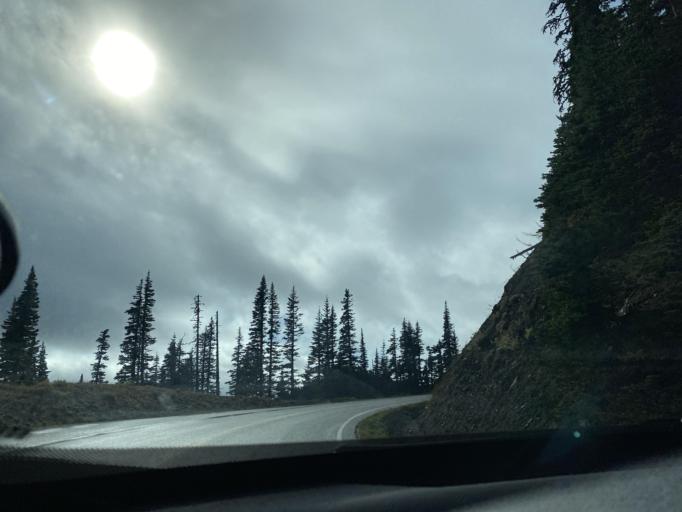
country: US
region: Washington
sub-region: Clallam County
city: Port Angeles
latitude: 47.9747
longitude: -123.4749
